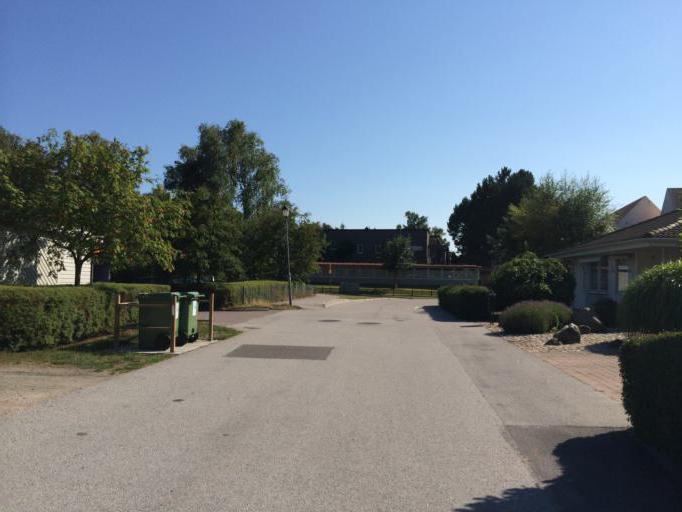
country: SE
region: Skane
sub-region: Vellinge Kommun
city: Skanor med Falsterbo
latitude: 55.4055
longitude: 12.8427
